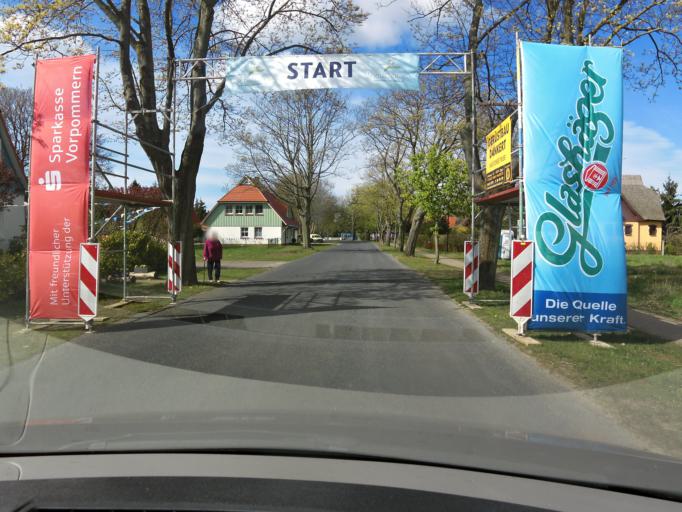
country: DE
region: Mecklenburg-Vorpommern
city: Ostseebad Prerow
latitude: 54.4112
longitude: 12.5818
